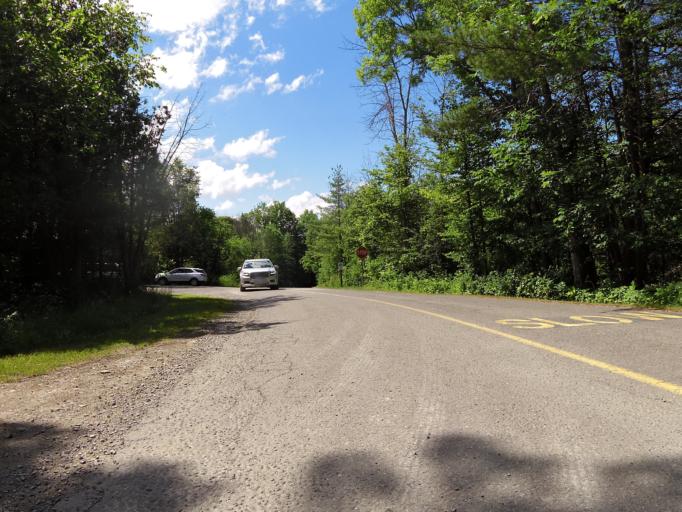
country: CA
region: Ontario
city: Arnprior
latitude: 45.4838
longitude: -76.2203
